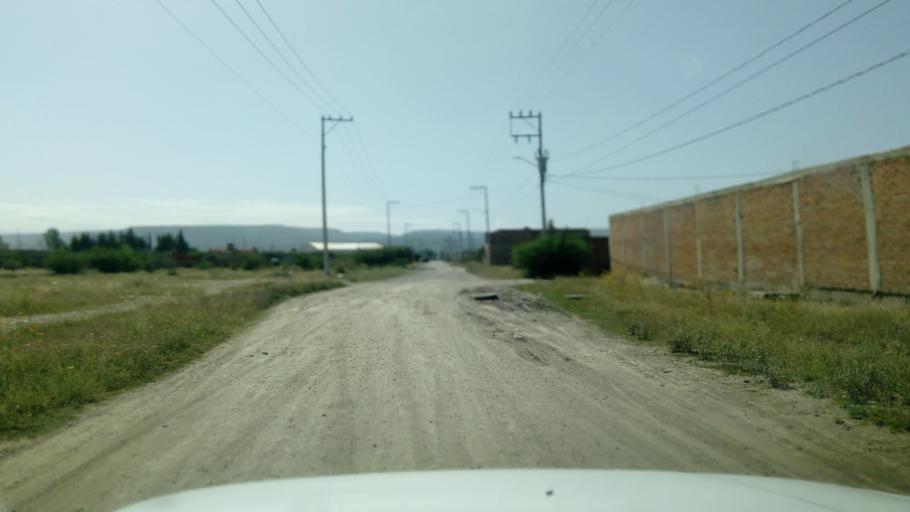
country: MX
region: Durango
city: Victoria de Durango
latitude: 23.9831
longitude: -104.6805
